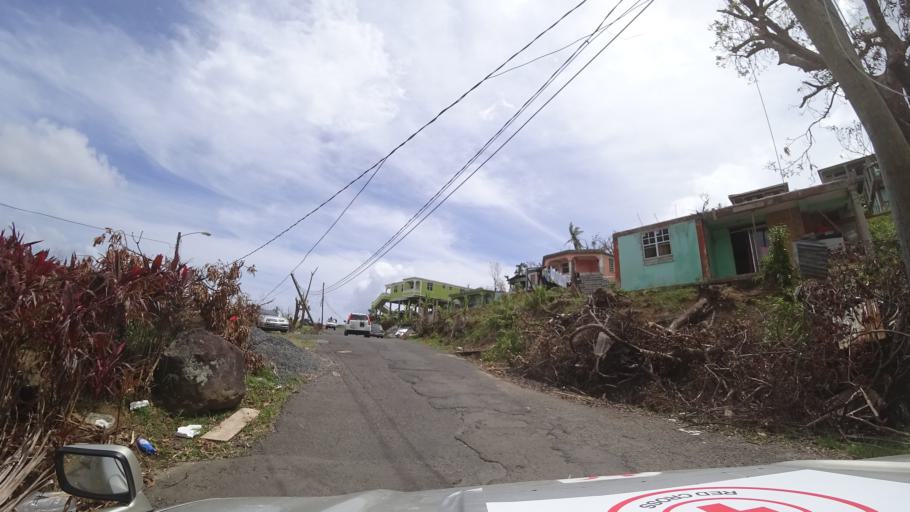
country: DM
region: Saint Patrick
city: Berekua
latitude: 15.2444
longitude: -61.3194
